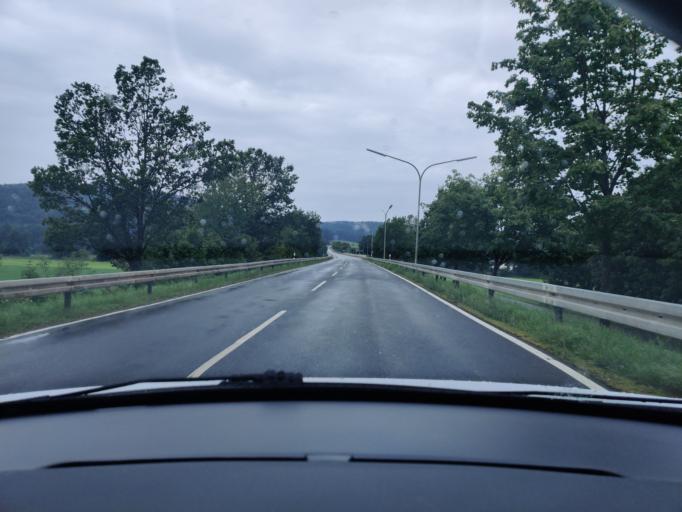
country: DE
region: Bavaria
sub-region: Upper Palatinate
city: Pfreimd
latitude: 49.4958
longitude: 12.1771
